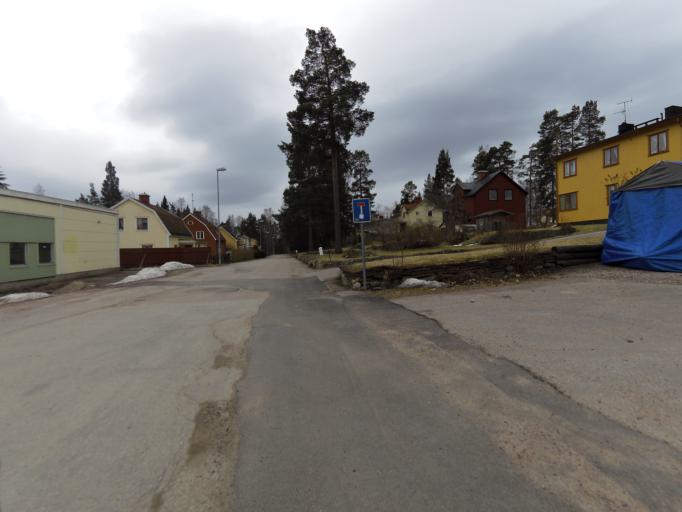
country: SE
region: Gaevleborg
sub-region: Hofors Kommun
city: Hofors
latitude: 60.5488
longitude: 16.2814
